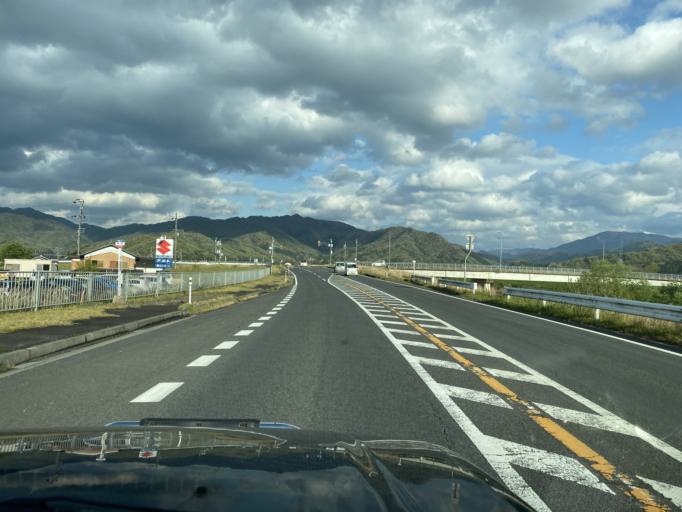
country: JP
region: Hyogo
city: Toyooka
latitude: 35.4896
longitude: 134.8472
